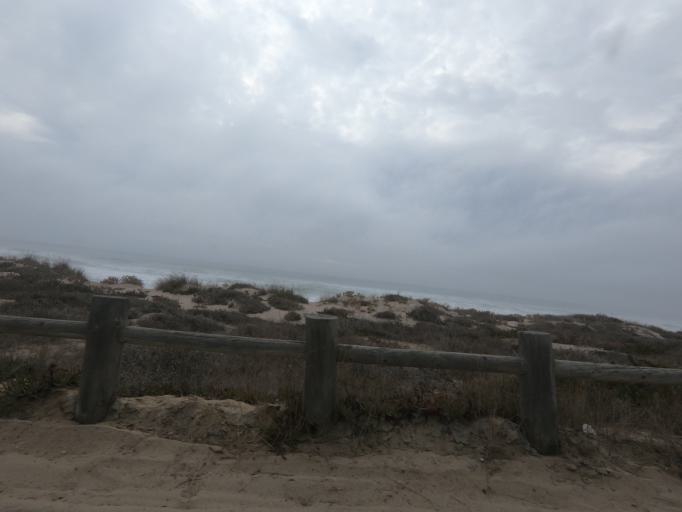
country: PT
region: Setubal
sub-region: Almada
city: Charneca
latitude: 38.5631
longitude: -9.1914
